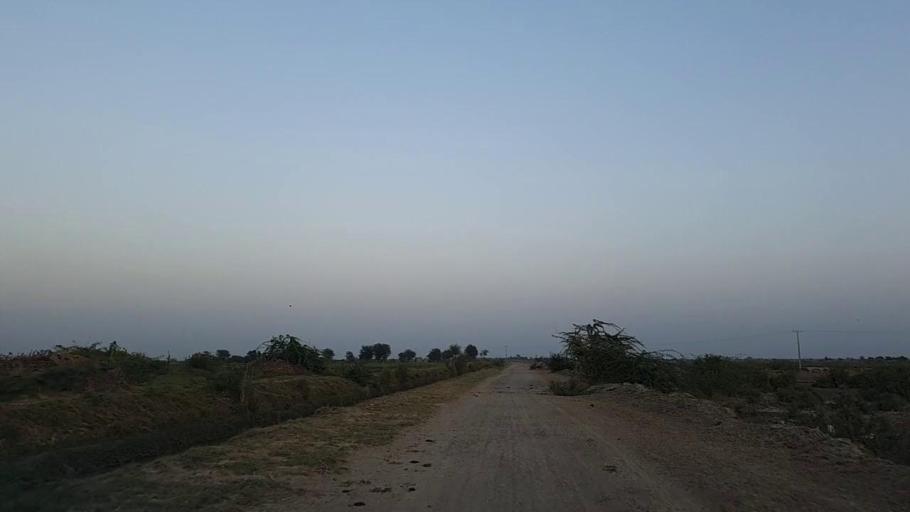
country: PK
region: Sindh
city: Pithoro
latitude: 25.4148
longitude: 69.3124
